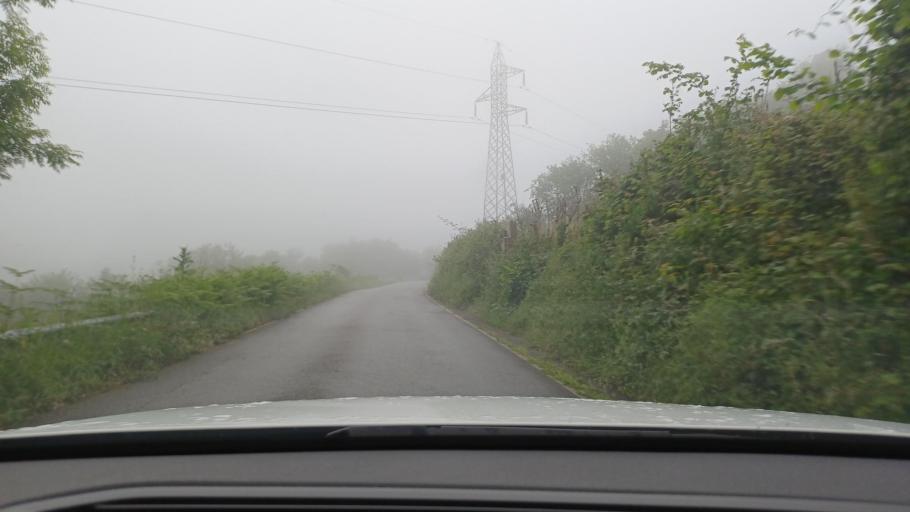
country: ES
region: Asturias
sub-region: Province of Asturias
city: Proaza
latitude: 43.2926
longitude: -5.9648
